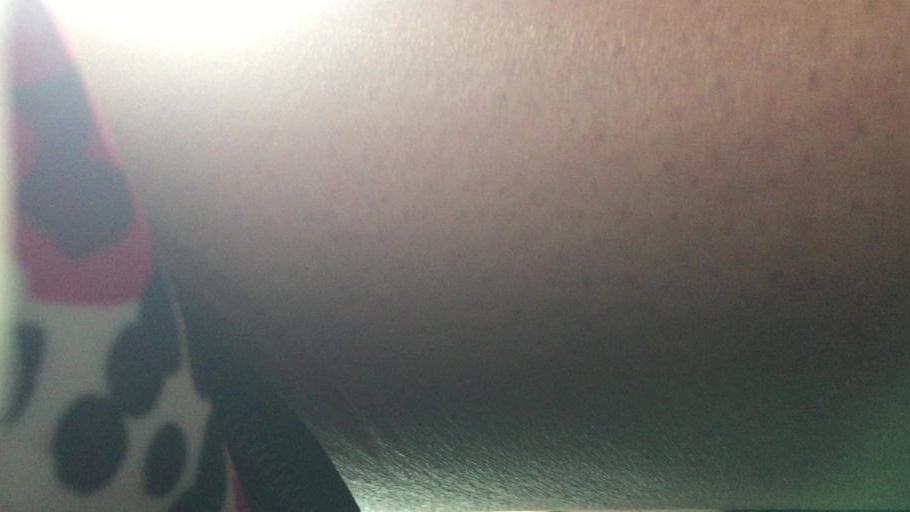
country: US
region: Georgia
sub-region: Carroll County
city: Carrollton
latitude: 33.5940
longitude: -85.0414
